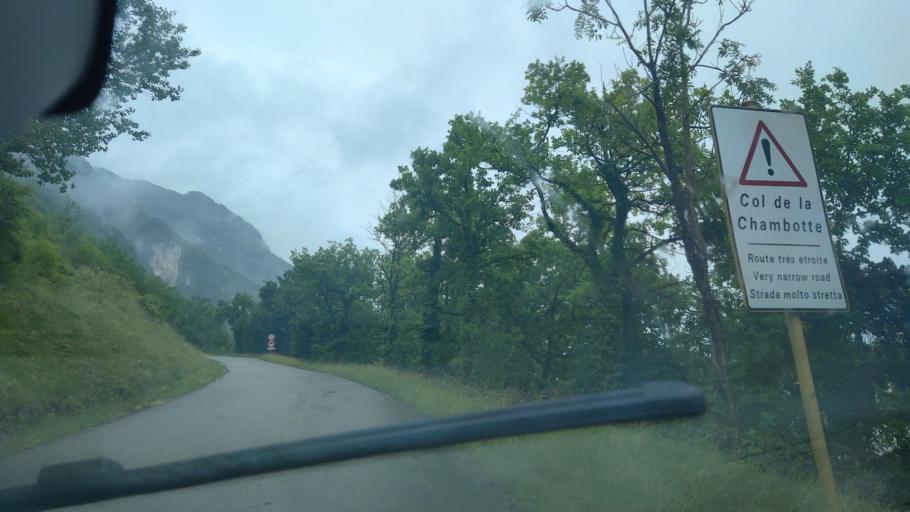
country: FR
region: Rhone-Alpes
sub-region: Departement de la Savoie
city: Chatillon
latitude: 45.8047
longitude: 5.8582
